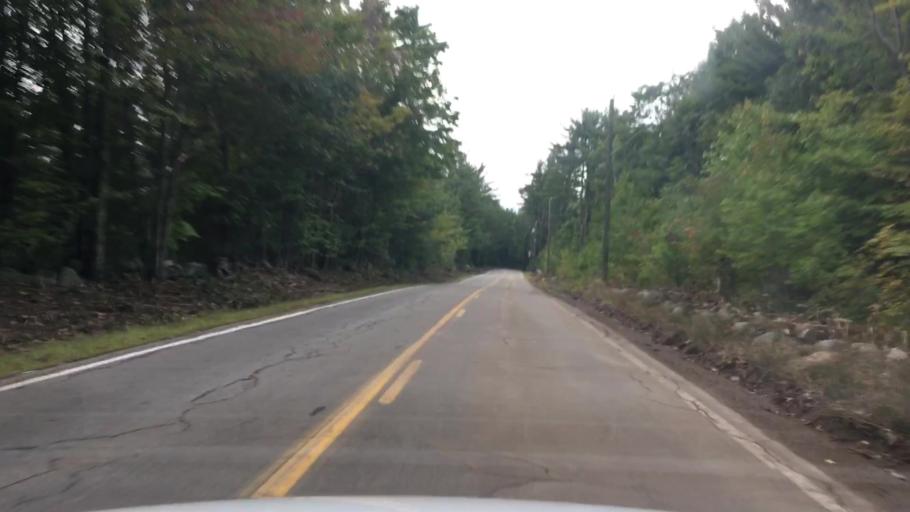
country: US
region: New Hampshire
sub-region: Carroll County
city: Effingham
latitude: 43.7706
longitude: -70.9974
